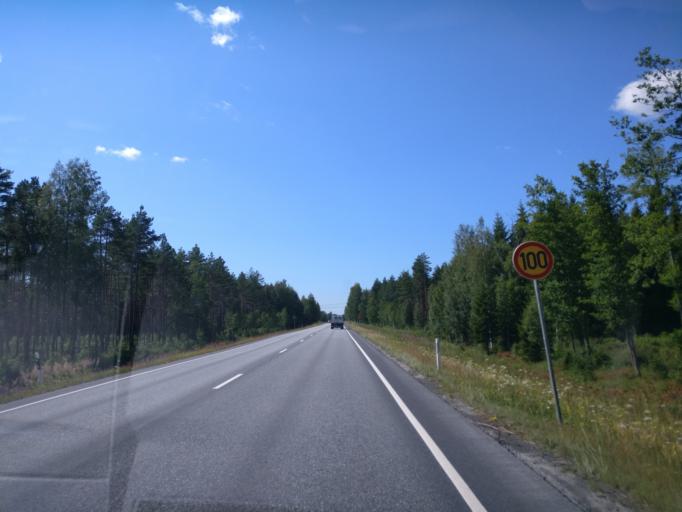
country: FI
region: Satakunta
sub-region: Pori
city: Kullaa
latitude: 61.4591
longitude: 22.0833
